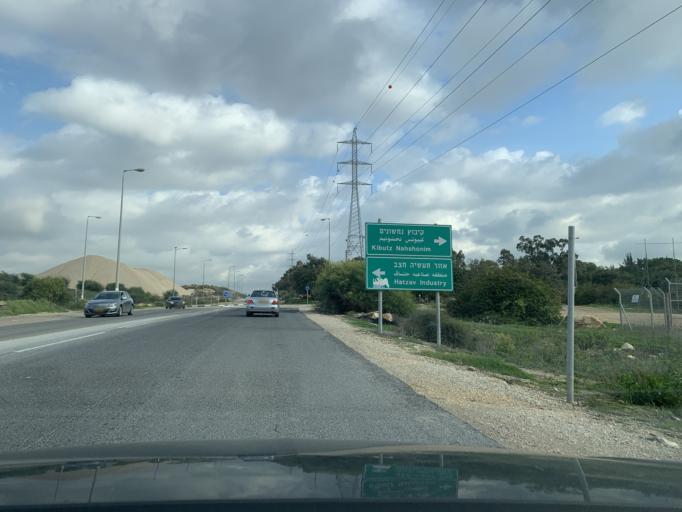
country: IL
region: Central District
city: Rosh Ha'Ayin
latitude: 32.0670
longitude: 34.9463
